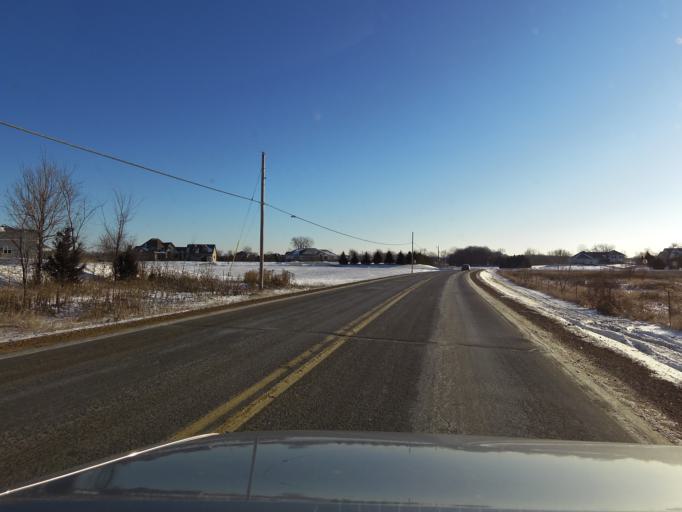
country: US
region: Minnesota
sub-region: Scott County
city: Shakopee
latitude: 44.7328
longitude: -93.5334
